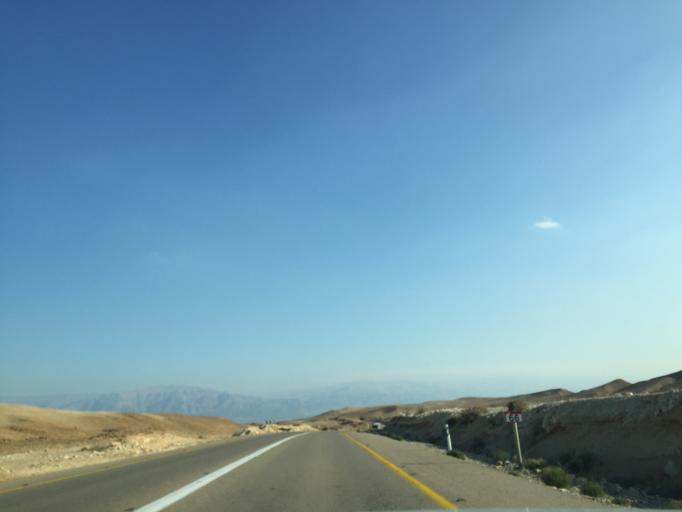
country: IL
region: Southern District
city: `En Boqeq
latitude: 31.1673
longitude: 35.3187
